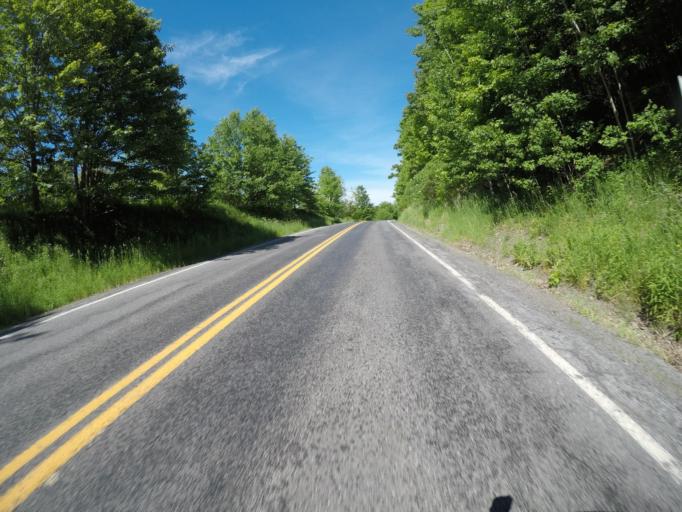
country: US
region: New York
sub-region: Delaware County
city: Delhi
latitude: 42.2121
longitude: -74.9150
